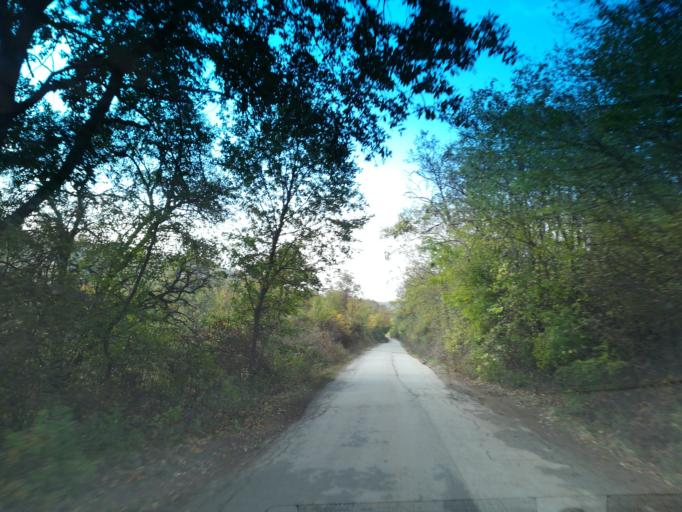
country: BG
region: Stara Zagora
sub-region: Obshtina Nikolaevo
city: Elkhovo
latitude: 42.3309
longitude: 25.4035
